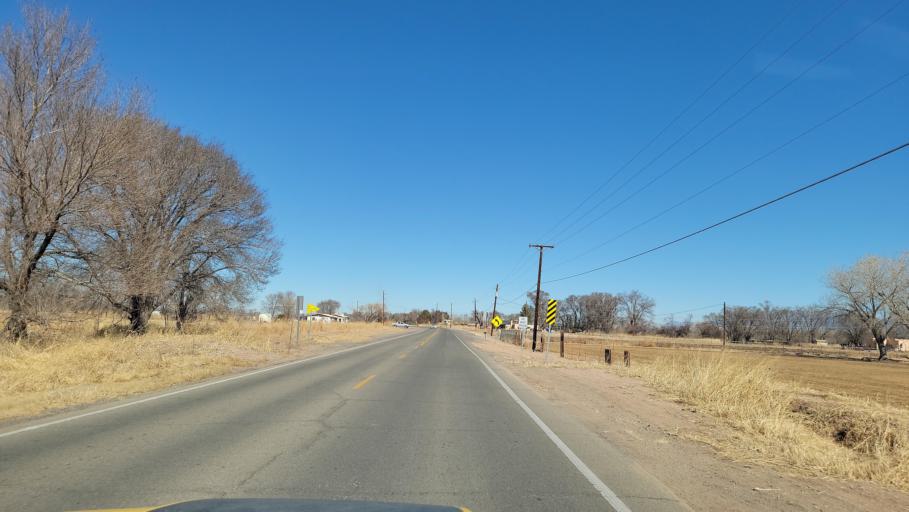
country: US
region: New Mexico
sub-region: Bernalillo County
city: South Valley
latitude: 34.9357
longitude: -106.6919
